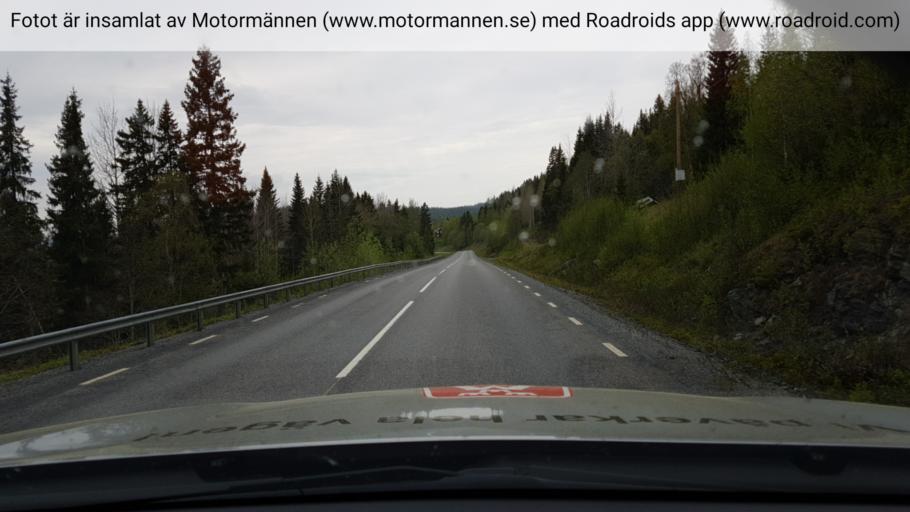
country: SE
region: Jaemtland
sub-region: Are Kommun
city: Are
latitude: 63.5230
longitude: 13.1141
